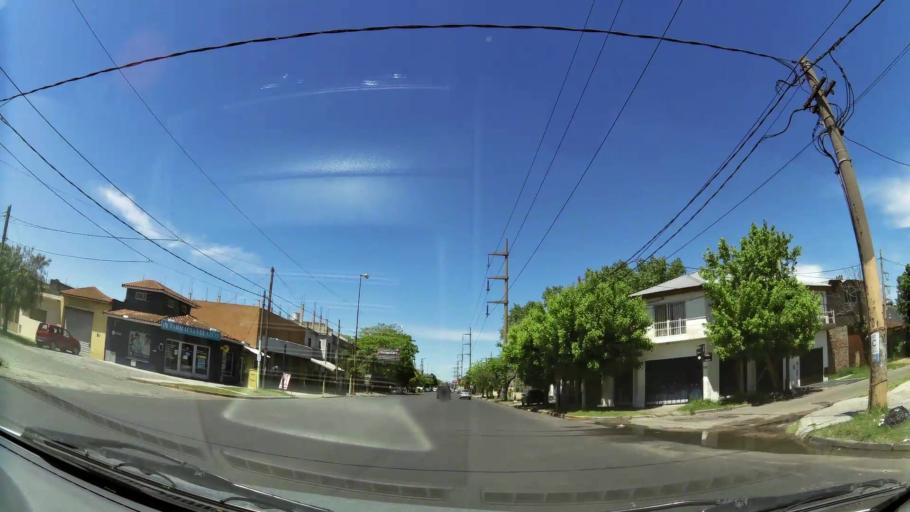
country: AR
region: Buenos Aires
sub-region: Partido de Quilmes
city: Quilmes
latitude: -34.7374
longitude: -58.2772
